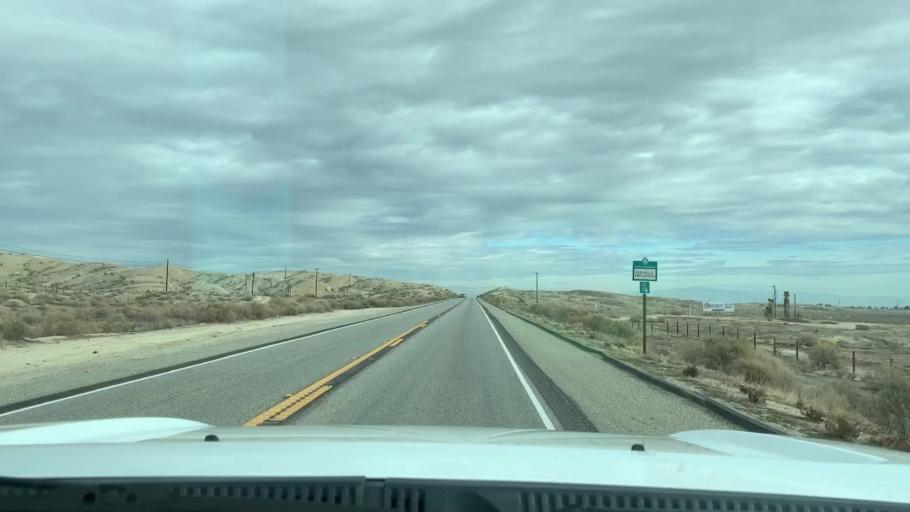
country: US
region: California
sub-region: Kern County
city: Ford City
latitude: 35.2330
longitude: -119.3699
